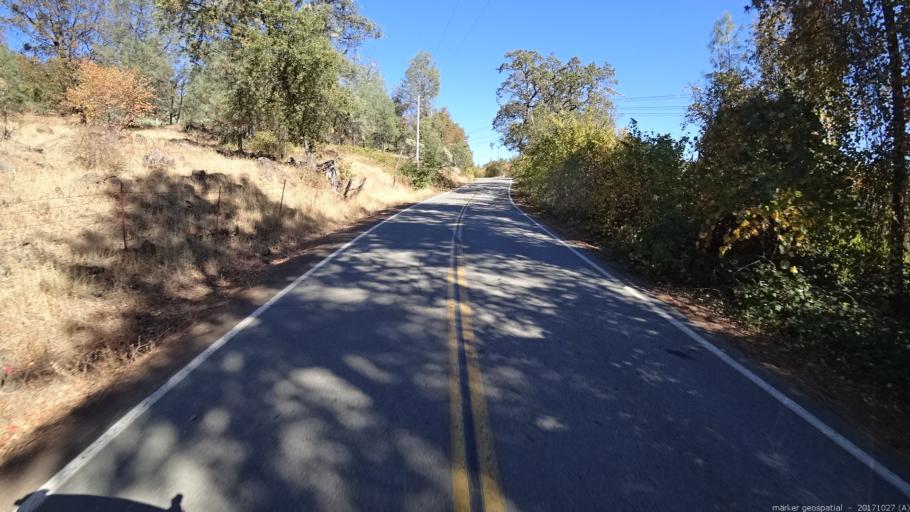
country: US
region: California
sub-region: Shasta County
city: Bella Vista
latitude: 40.7190
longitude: -122.0294
